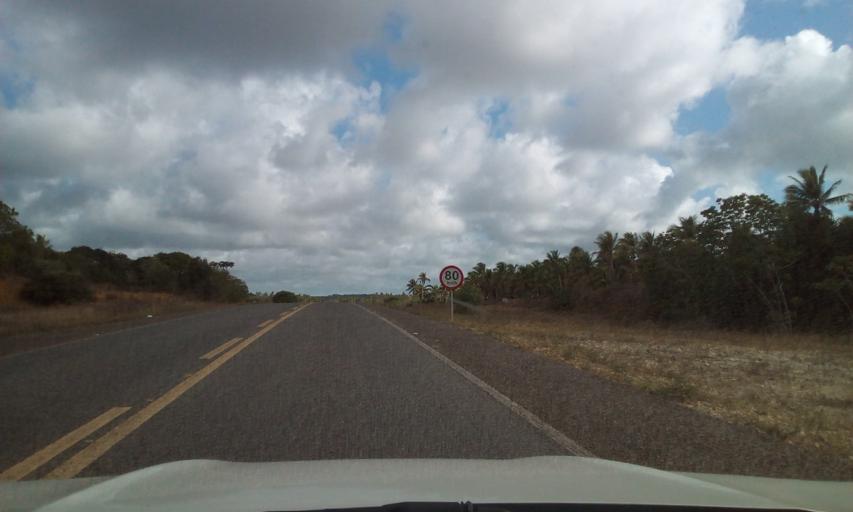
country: BR
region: Sergipe
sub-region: Indiaroba
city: Indiaroba
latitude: -11.6362
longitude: -37.5397
